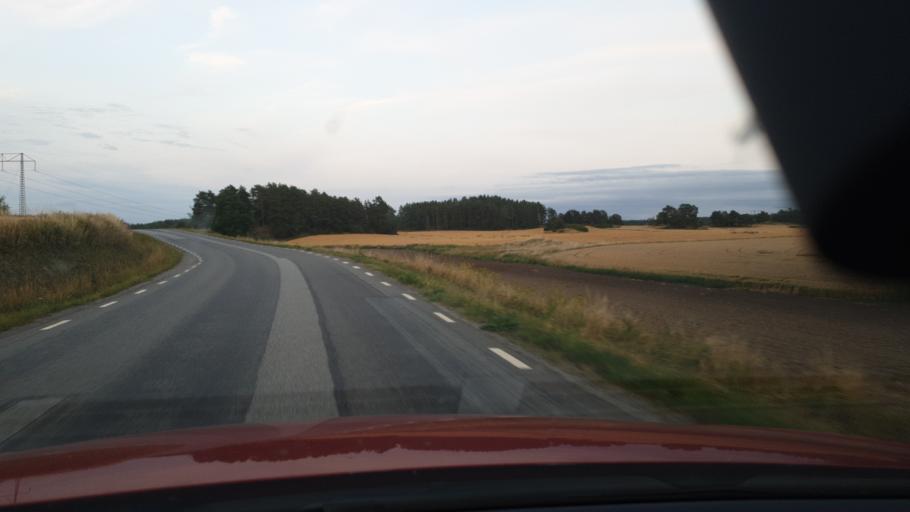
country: SE
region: Uppsala
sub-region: Enkopings Kommun
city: Orsundsbro
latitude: 59.6757
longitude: 17.4194
